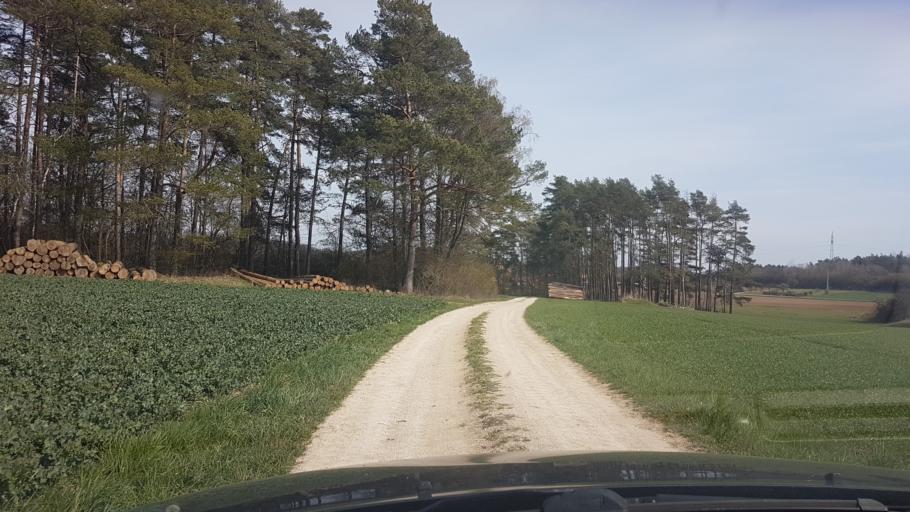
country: DE
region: Bavaria
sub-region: Upper Franconia
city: Wattendorf
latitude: 49.9949
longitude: 11.1246
